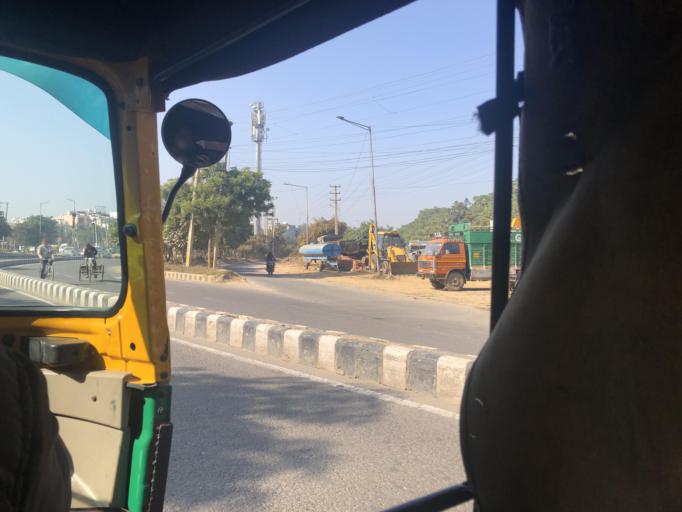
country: IN
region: Haryana
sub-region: Gurgaon
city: Gurgaon
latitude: 28.4461
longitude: 77.0774
